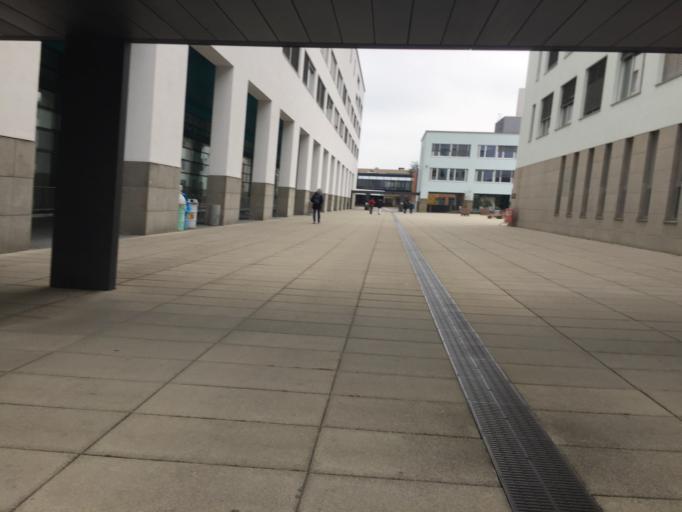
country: CH
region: Vaud
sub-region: Ouest Lausannois District
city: Ecublens
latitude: 46.5213
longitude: 6.5651
